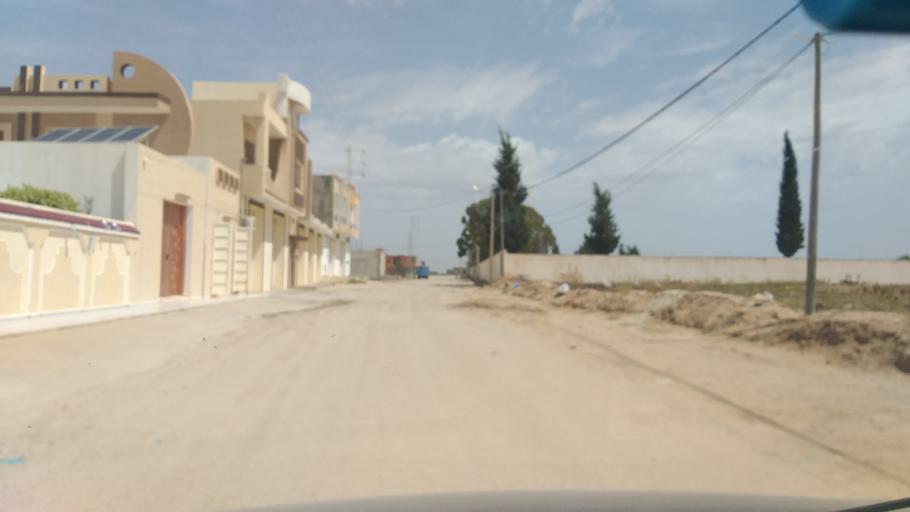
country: TN
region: Al Mahdiyah
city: El Jem
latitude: 35.3095
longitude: 10.7038
